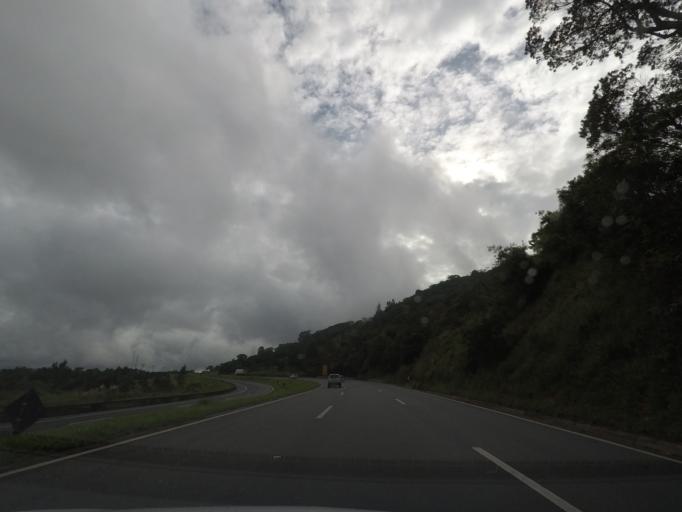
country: BR
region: Parana
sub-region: Campina Grande Do Sul
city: Campina Grande do Sul
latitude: -25.1524
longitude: -48.8599
